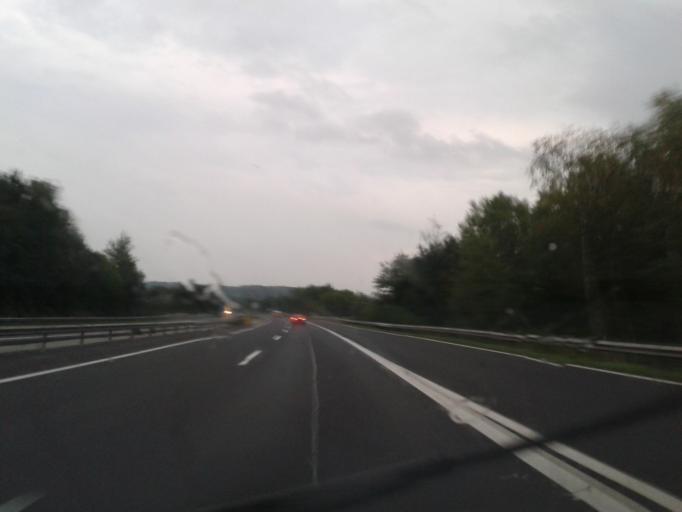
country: AT
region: Burgenland
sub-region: Politischer Bezirk Oberwart
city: Markt Allhau
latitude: 47.2830
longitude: 16.0647
